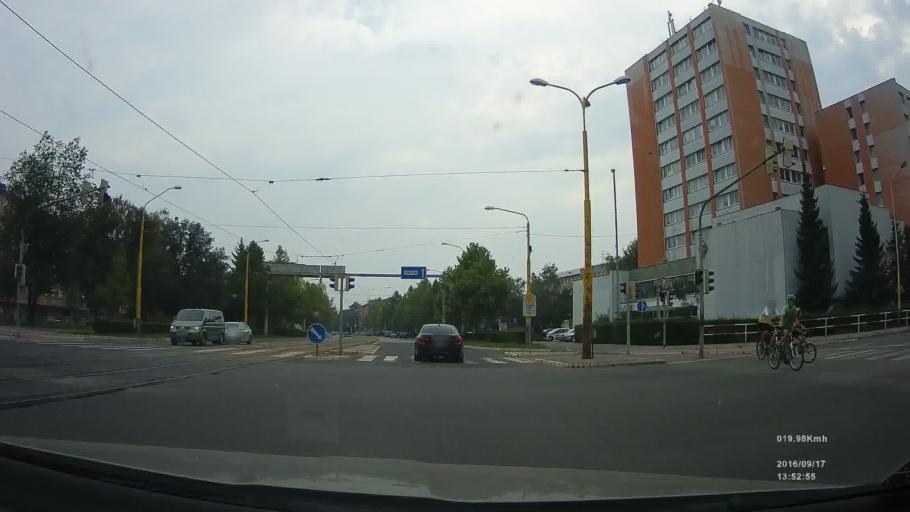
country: SK
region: Kosicky
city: Kosice
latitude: 48.7368
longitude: 21.2460
